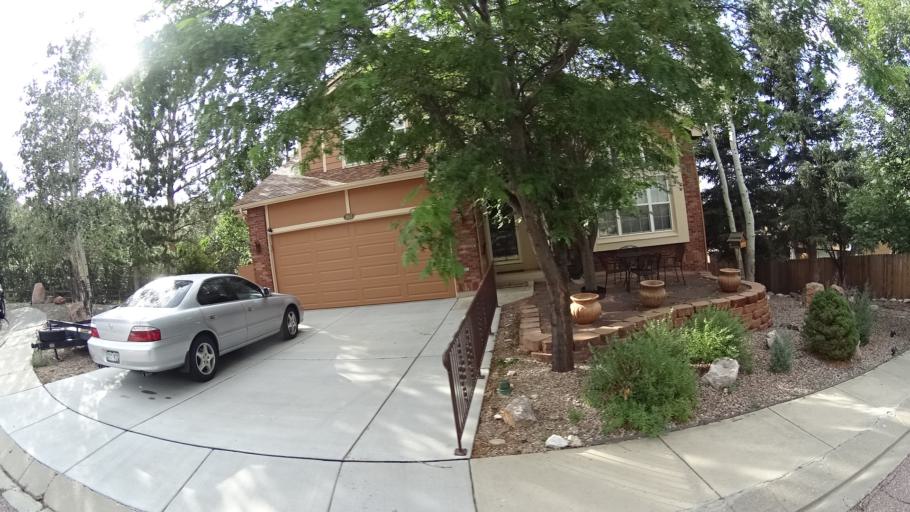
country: US
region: Colorado
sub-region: El Paso County
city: Manitou Springs
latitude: 38.9081
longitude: -104.8555
